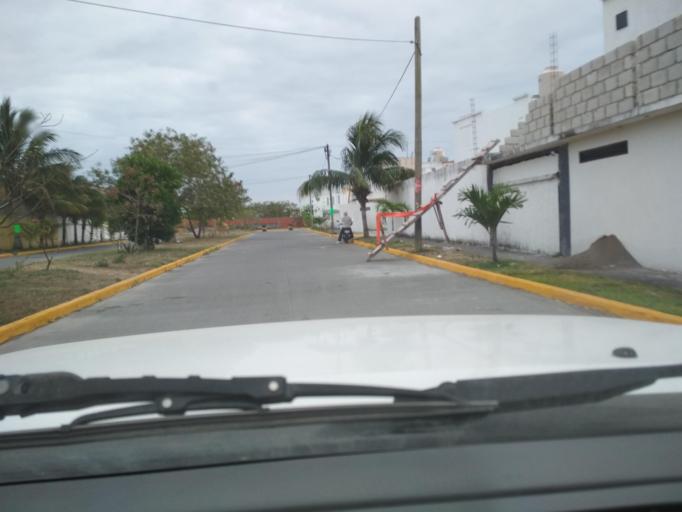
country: MX
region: Veracruz
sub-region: Medellin
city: Fraccionamiento Arboledas San Ramon
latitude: 19.0917
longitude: -96.1562
